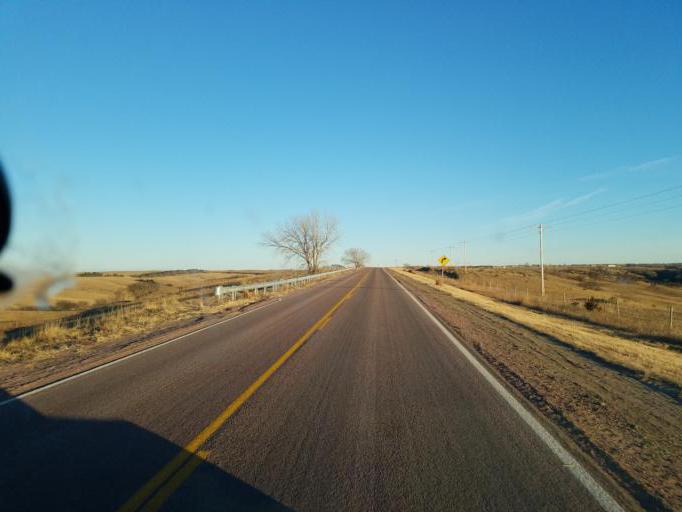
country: US
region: South Dakota
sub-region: Bon Homme County
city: Springfield
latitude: 42.7419
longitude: -97.9211
